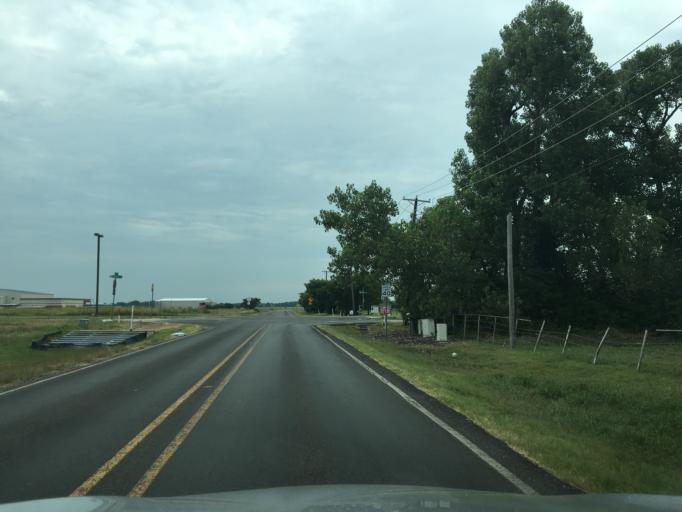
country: US
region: Texas
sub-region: Collin County
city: McKinney
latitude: 33.1718
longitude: -96.5994
